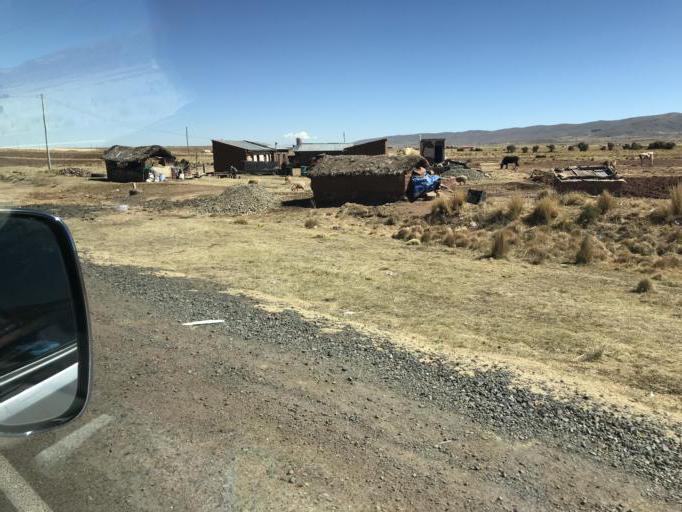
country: BO
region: La Paz
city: Tiahuanaco
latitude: -16.5943
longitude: -68.5740
